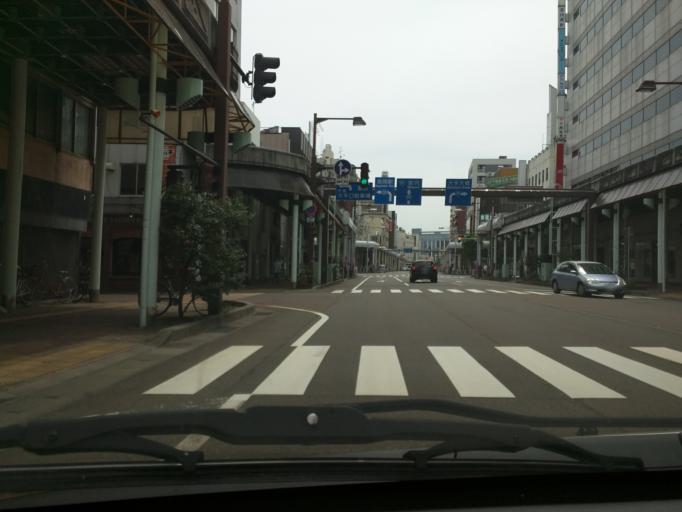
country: JP
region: Niigata
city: Nagaoka
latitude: 37.4485
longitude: 138.8510
